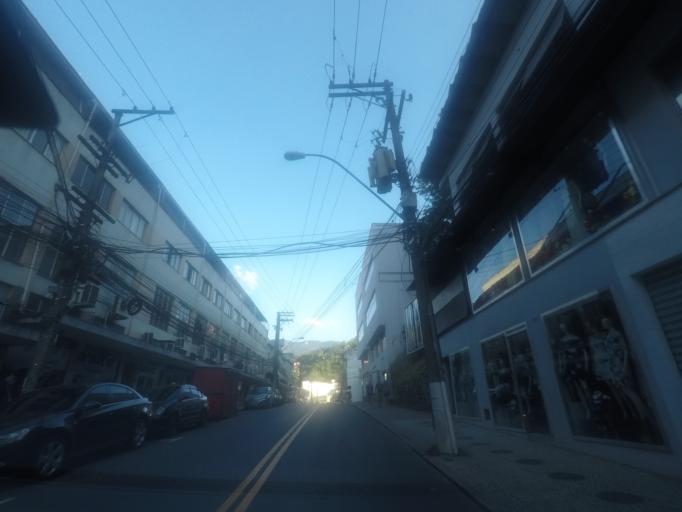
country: BR
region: Rio de Janeiro
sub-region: Petropolis
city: Petropolis
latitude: -22.5141
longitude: -43.1765
